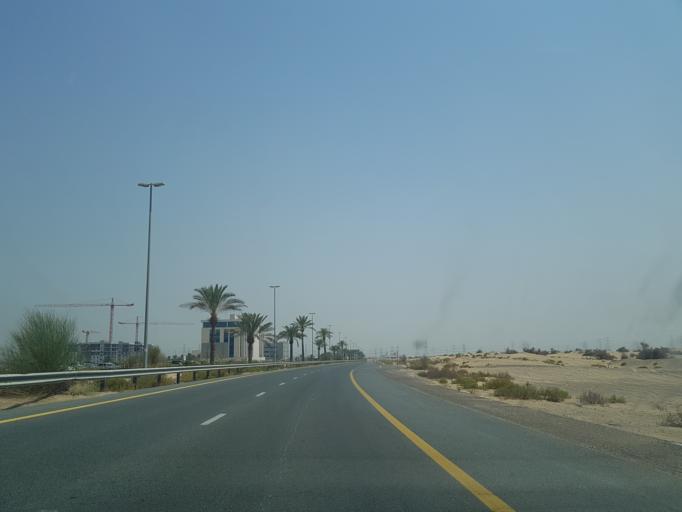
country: AE
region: Ash Shariqah
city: Sharjah
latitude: 25.1241
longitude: 55.4275
